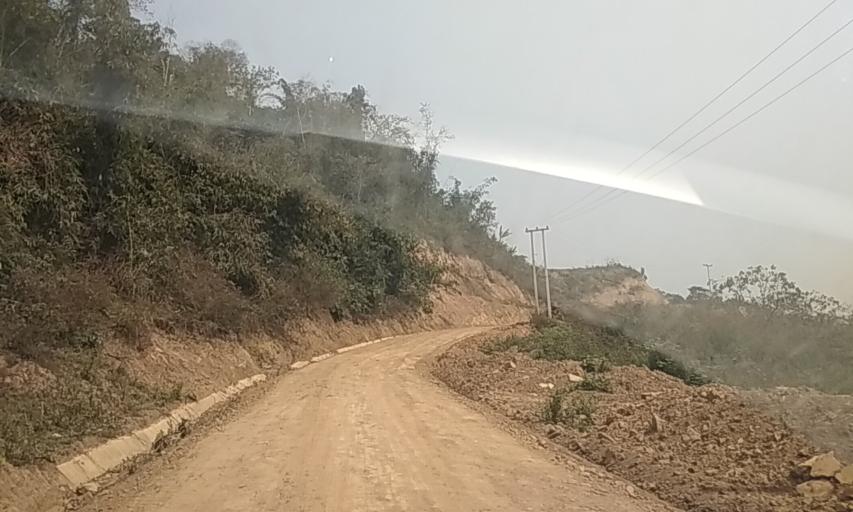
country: VN
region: Huyen Dien Bien
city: Dien Bien Phu
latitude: 21.4369
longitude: 102.7669
